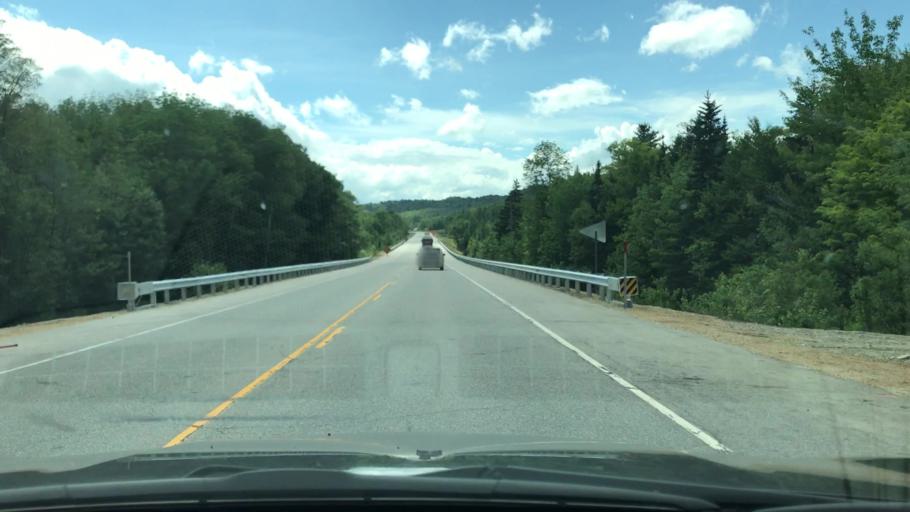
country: US
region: New Hampshire
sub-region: Coos County
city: Gorham
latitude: 44.3670
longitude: -71.3125
